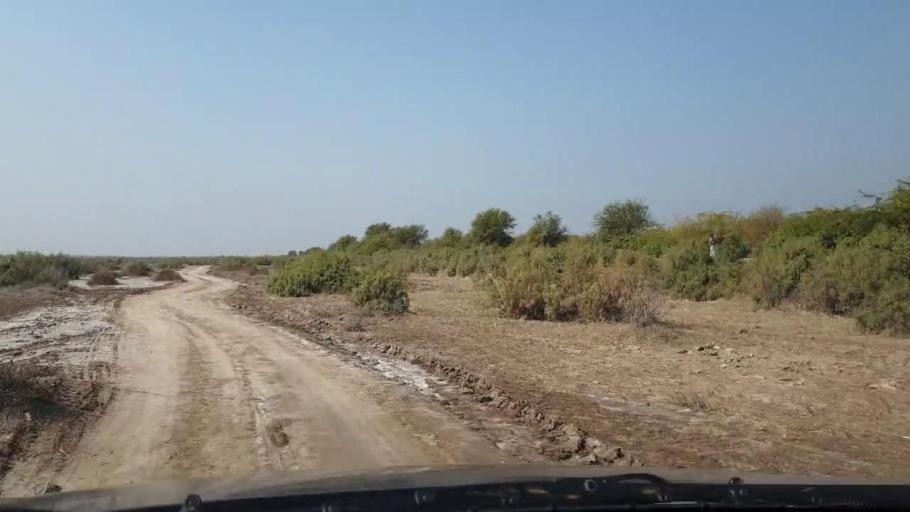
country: PK
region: Sindh
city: Jhol
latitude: 25.8885
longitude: 68.9779
